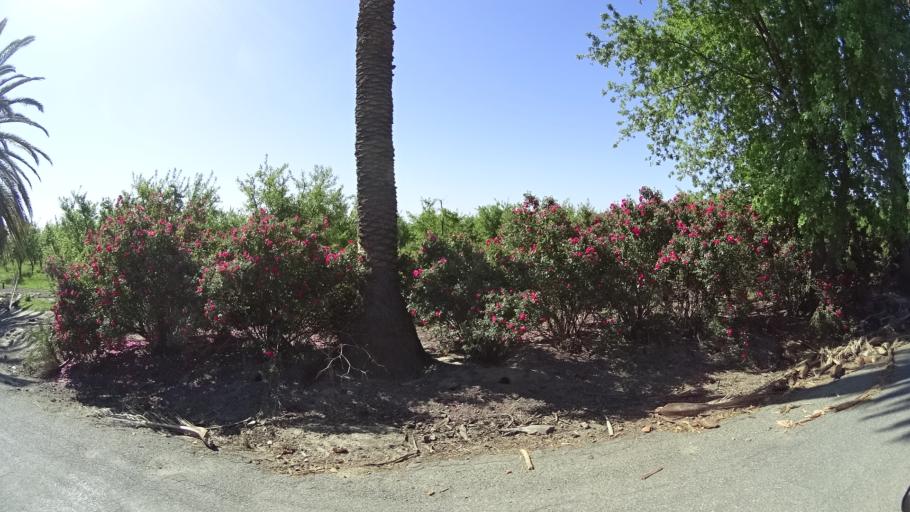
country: US
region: California
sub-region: Glenn County
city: Hamilton City
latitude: 39.7374
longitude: -122.0379
